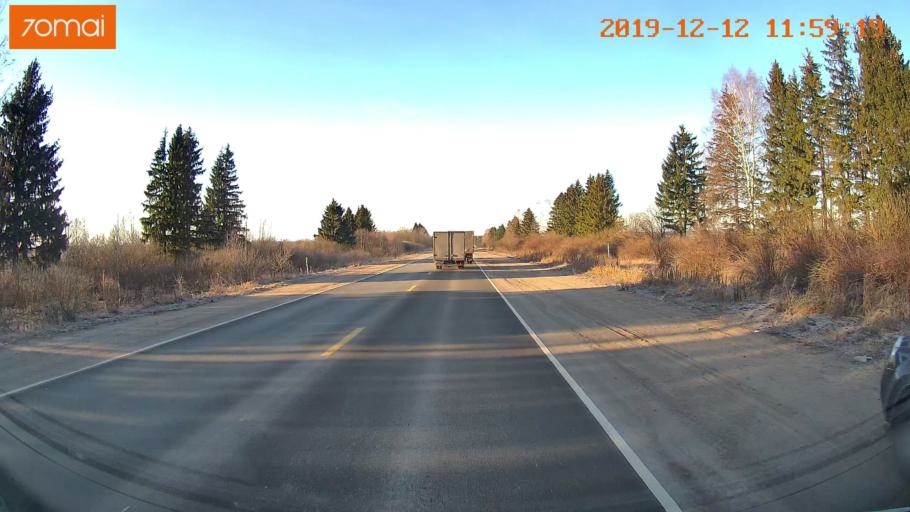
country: RU
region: Ivanovo
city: Kitovo
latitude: 56.8620
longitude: 41.3201
